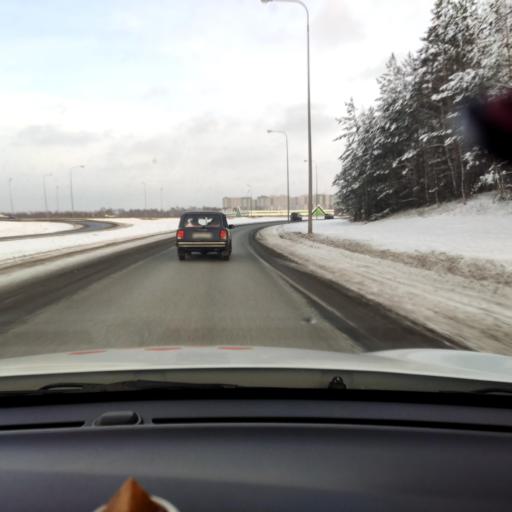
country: RU
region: Tatarstan
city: Osinovo
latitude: 55.8560
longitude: 48.8558
